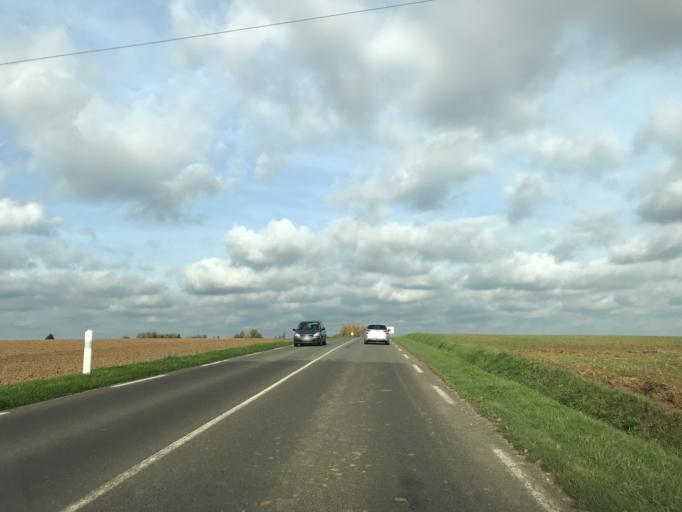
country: FR
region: Haute-Normandie
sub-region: Departement de l'Eure
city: Les Andelys
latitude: 49.2746
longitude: 1.4101
